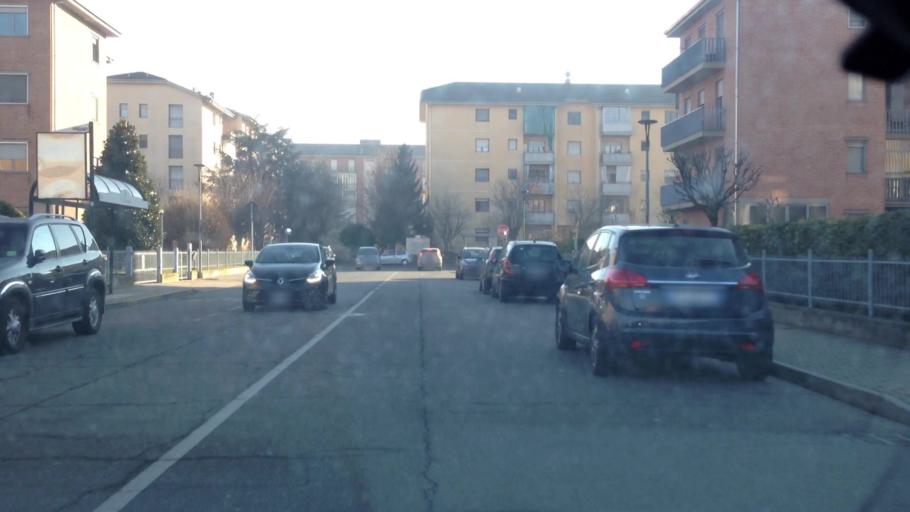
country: IT
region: Piedmont
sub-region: Provincia di Asti
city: Asti
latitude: 44.8953
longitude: 8.2184
